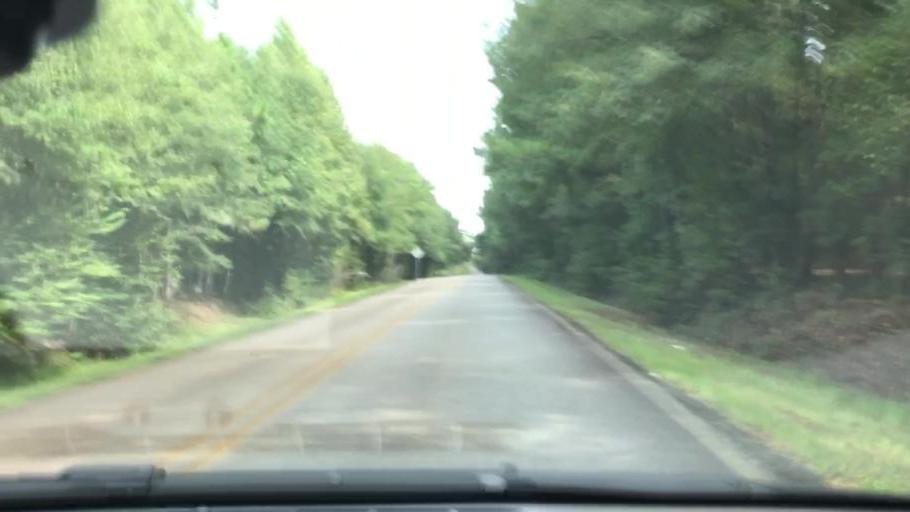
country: US
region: Georgia
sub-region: Clay County
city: Fort Gaines
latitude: 31.5708
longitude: -85.0011
